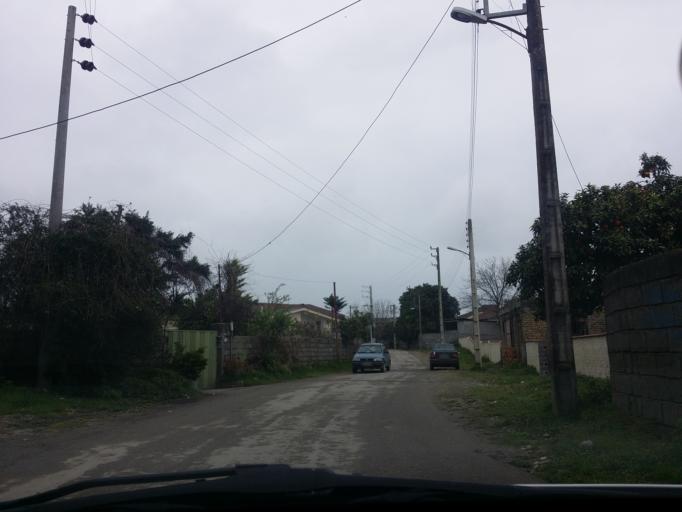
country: IR
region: Mazandaran
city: Chalus
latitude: 36.6664
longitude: 51.3806
